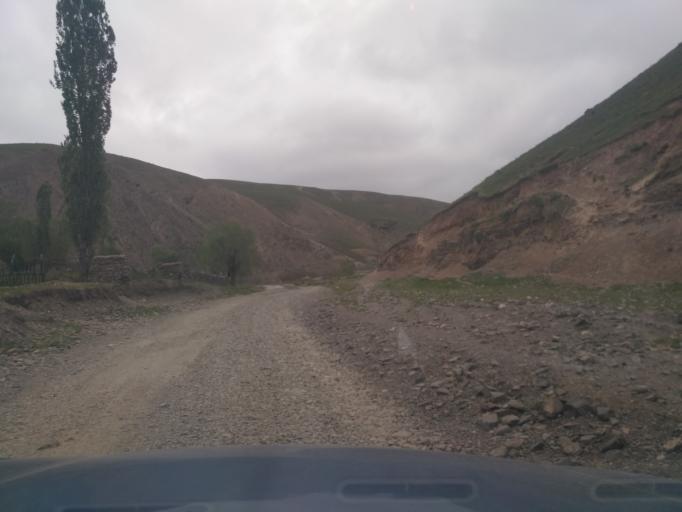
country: UZ
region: Jizzax
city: Zomin
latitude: 39.8460
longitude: 68.4009
